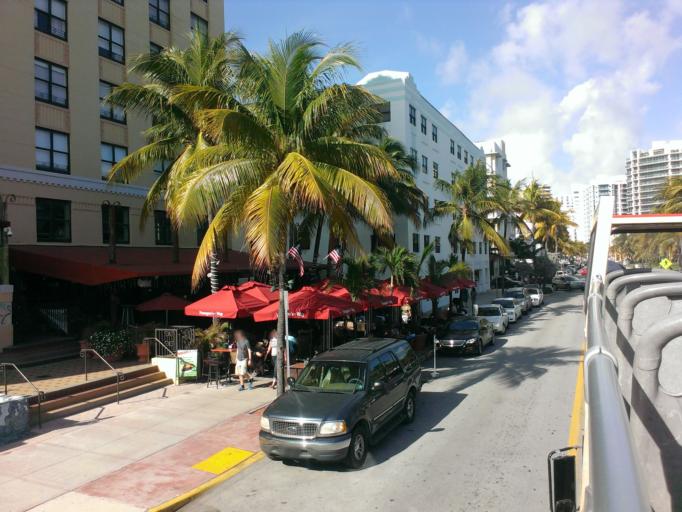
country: US
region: Florida
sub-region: Miami-Dade County
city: Miami Beach
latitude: 25.7845
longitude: -80.1299
